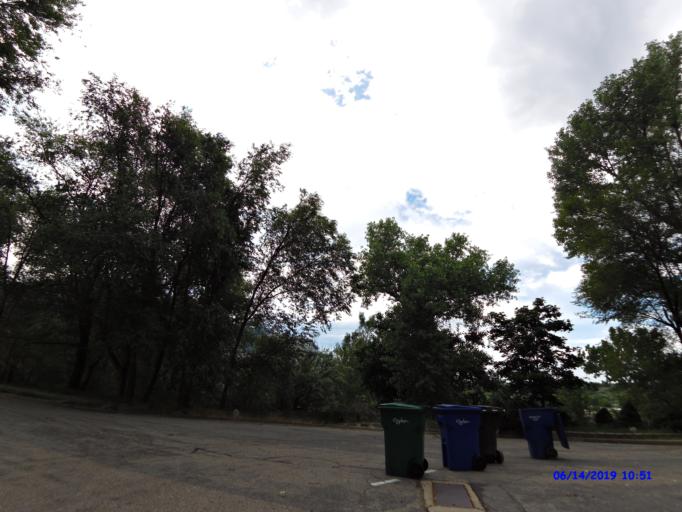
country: US
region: Utah
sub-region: Weber County
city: Ogden
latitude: 41.2444
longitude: -111.9442
